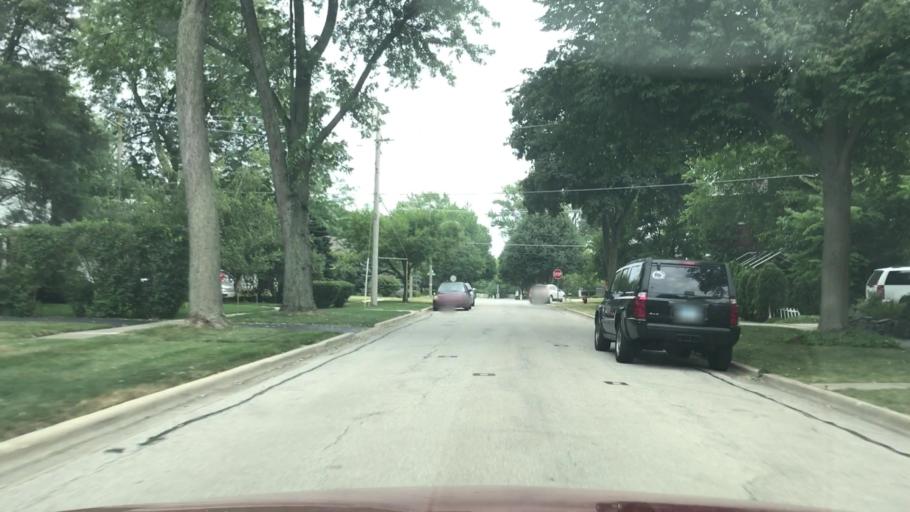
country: US
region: Illinois
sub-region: Cook County
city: Arlington Heights
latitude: 42.0693
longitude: -87.9879
